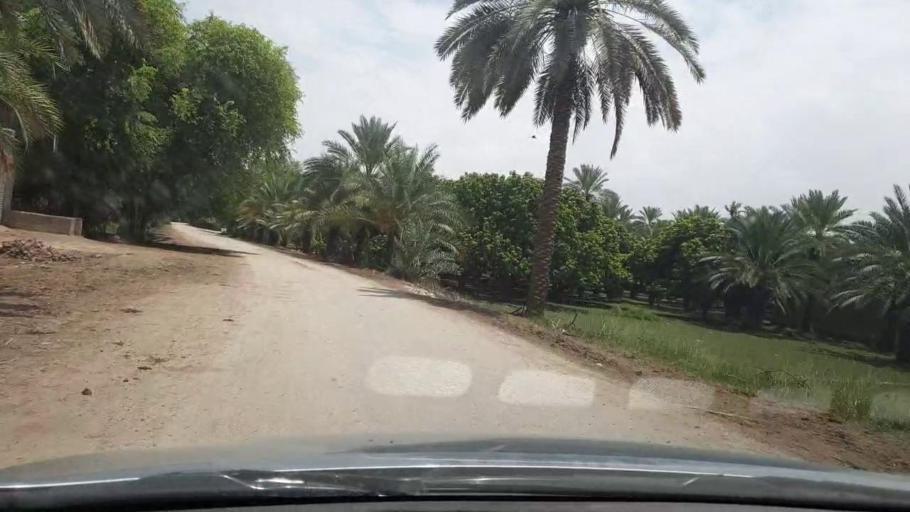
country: PK
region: Sindh
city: Khairpur
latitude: 27.4321
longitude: 68.7717
